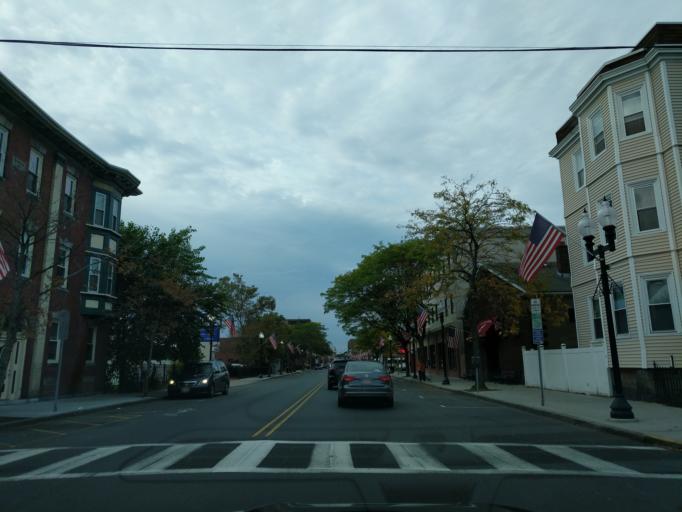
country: US
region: Massachusetts
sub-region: Suffolk County
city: Revere
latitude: 42.4118
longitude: -71.0112
